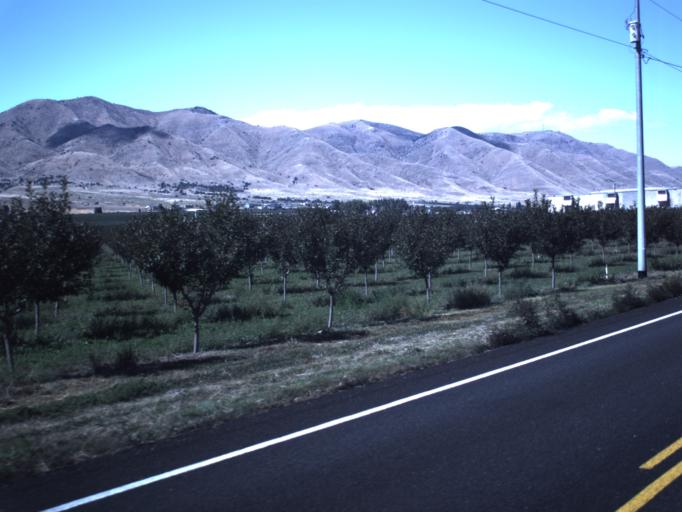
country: US
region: Utah
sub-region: Utah County
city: West Mountain
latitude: 40.0307
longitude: -111.7871
